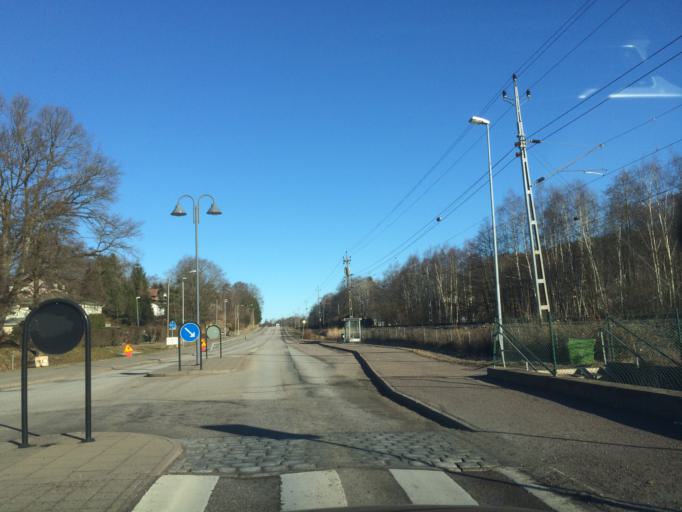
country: SE
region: Vaestra Goetaland
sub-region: Molndal
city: Lindome
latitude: 57.5795
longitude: 12.0764
